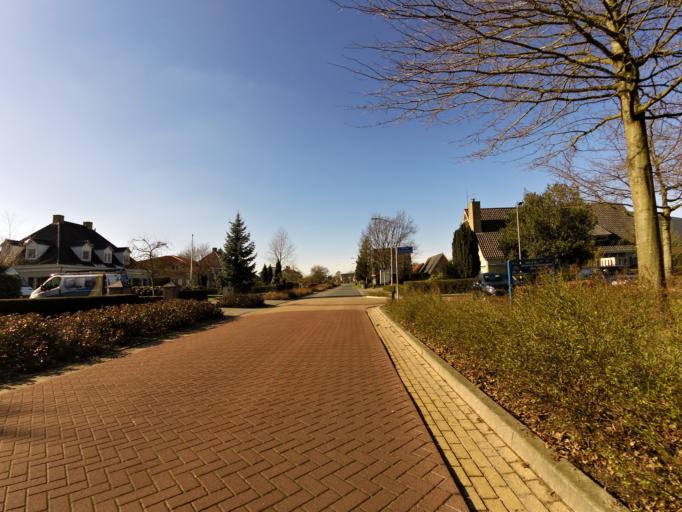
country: NL
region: Gelderland
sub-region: Gemeente Doesburg
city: Doesburg
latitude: 51.9630
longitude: 6.2043
